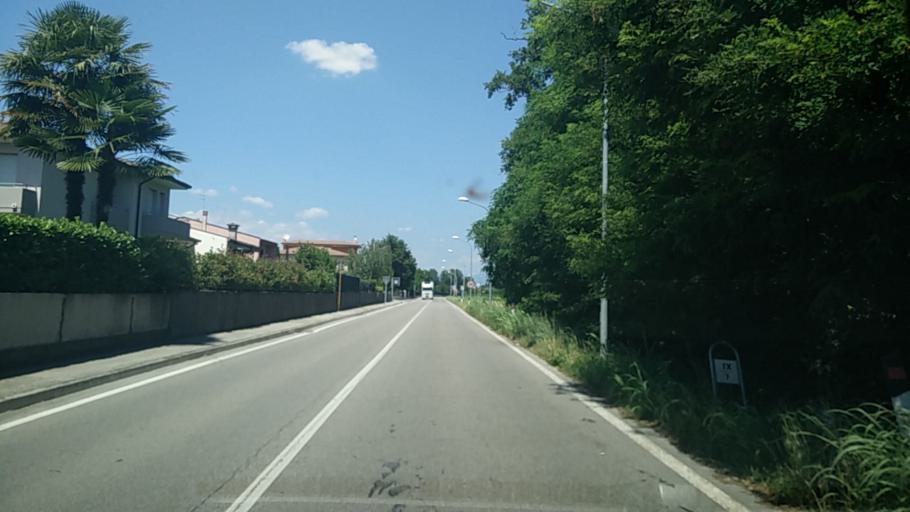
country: IT
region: Veneto
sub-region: Provincia di Padova
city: Tombolo
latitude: 45.6293
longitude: 11.8202
